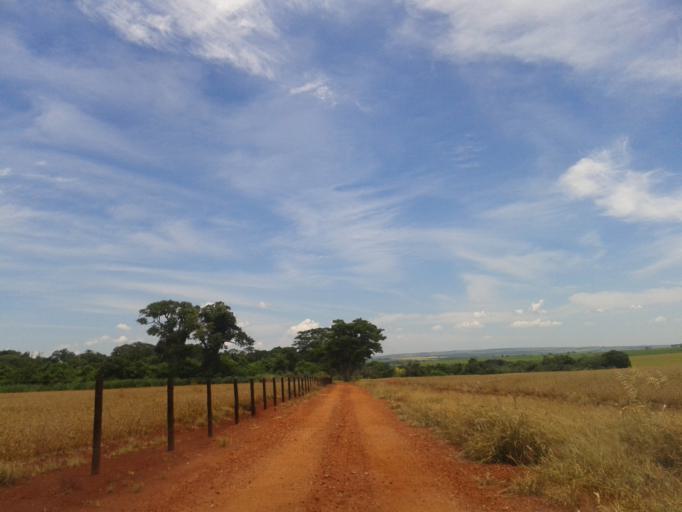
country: BR
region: Minas Gerais
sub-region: Capinopolis
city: Capinopolis
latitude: -18.6629
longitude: -49.7307
